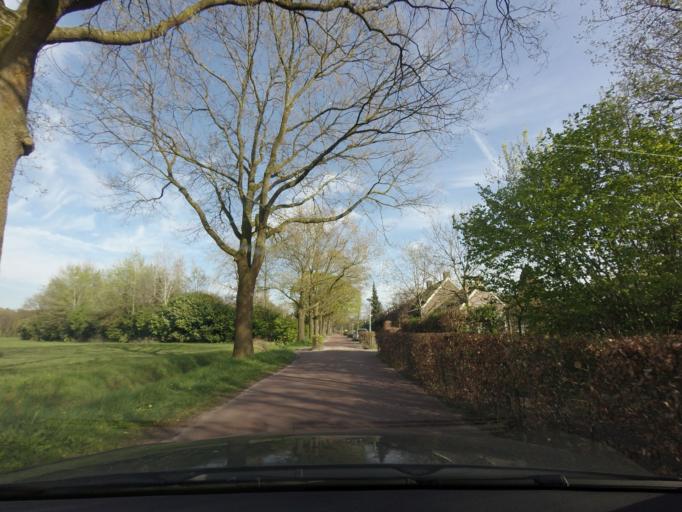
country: NL
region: North Brabant
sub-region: Gemeente Eindhoven
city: De Doornakkers
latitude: 51.4251
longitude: 5.5209
